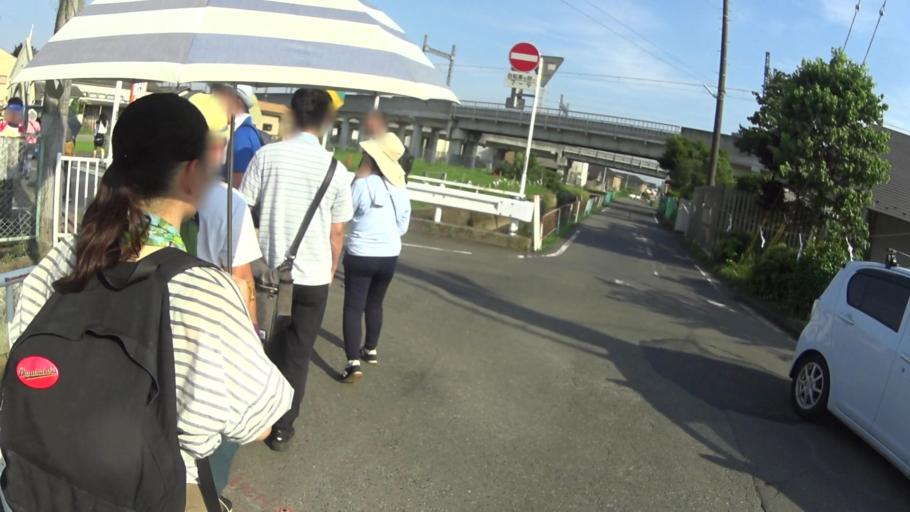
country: JP
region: Gunma
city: Ota
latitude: 36.2952
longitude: 139.3707
